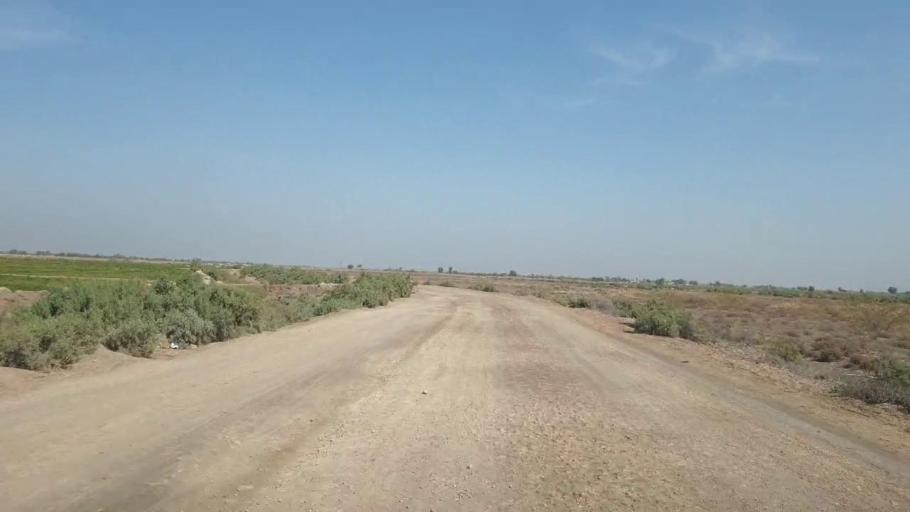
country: PK
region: Sindh
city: Samaro
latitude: 25.3541
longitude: 69.2535
